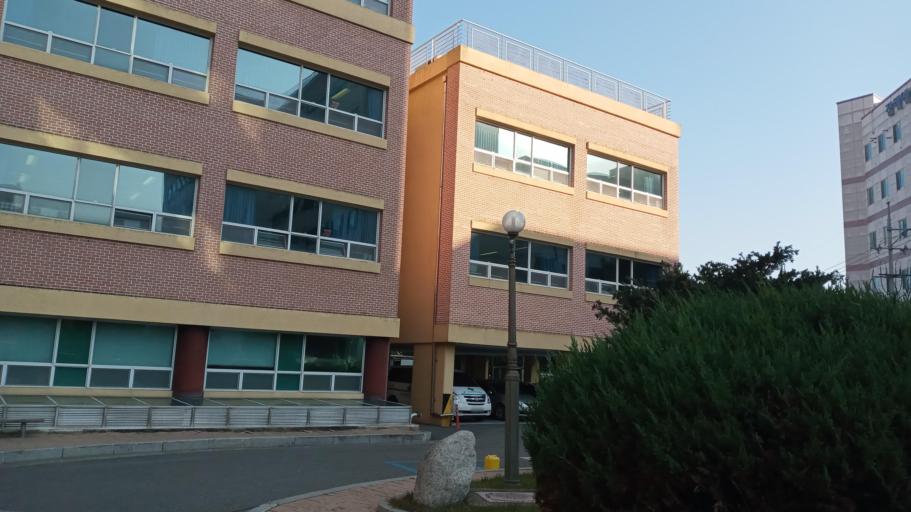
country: KR
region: Gyeongsangbuk-do
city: Gyeongsan-si
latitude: 35.8093
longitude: 128.7392
